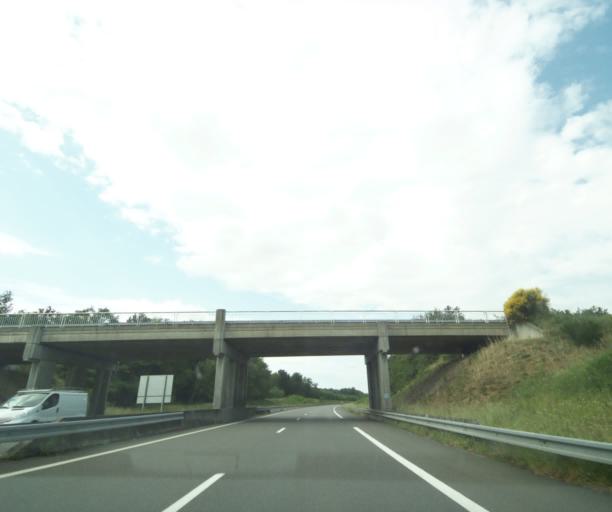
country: FR
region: Pays de la Loire
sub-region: Departement de Maine-et-Loire
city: Brion
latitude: 47.4426
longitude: -0.1757
